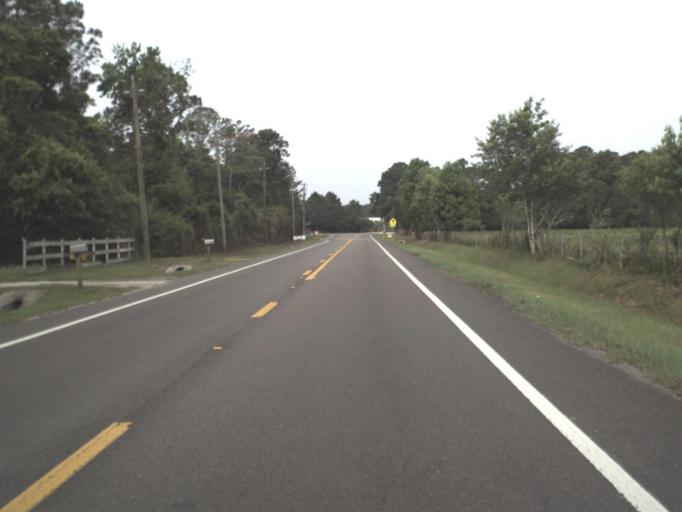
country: US
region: Florida
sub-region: Clay County
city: Green Cove Springs
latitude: 29.9745
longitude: -81.5160
